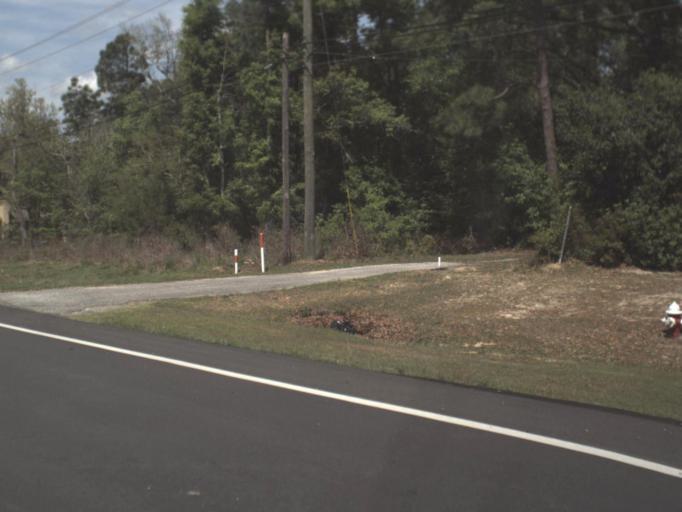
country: US
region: Florida
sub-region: Escambia County
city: Ensley
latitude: 30.5327
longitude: -87.2450
